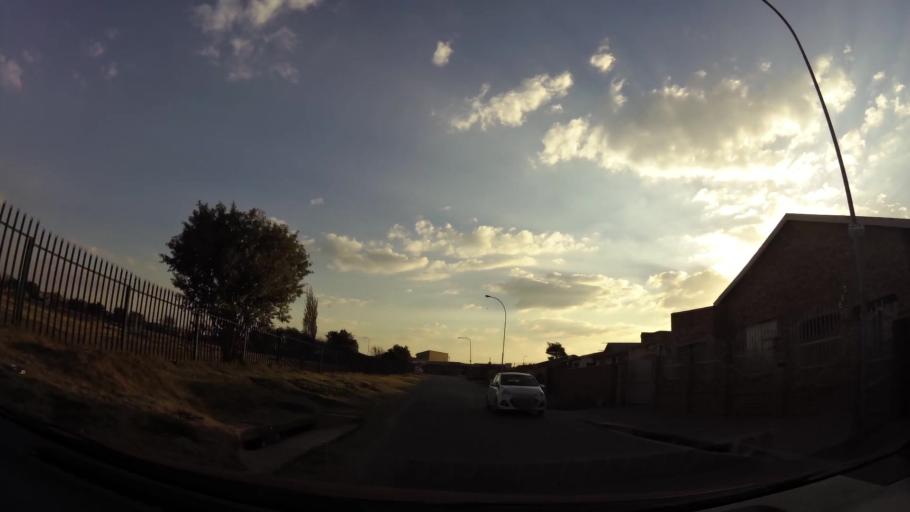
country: ZA
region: Gauteng
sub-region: City of Johannesburg Metropolitan Municipality
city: Roodepoort
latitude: -26.2107
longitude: 27.8982
